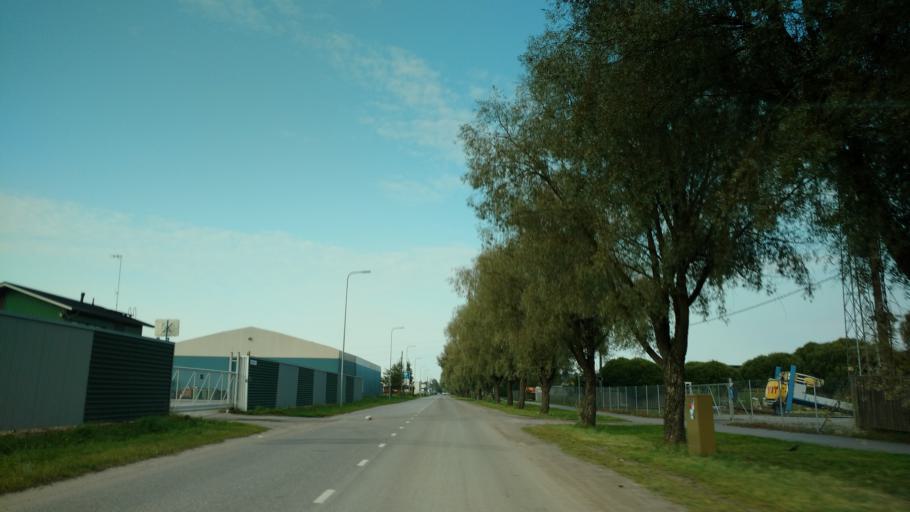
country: FI
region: Varsinais-Suomi
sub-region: Salo
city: Salo
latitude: 60.3726
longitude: 23.1043
